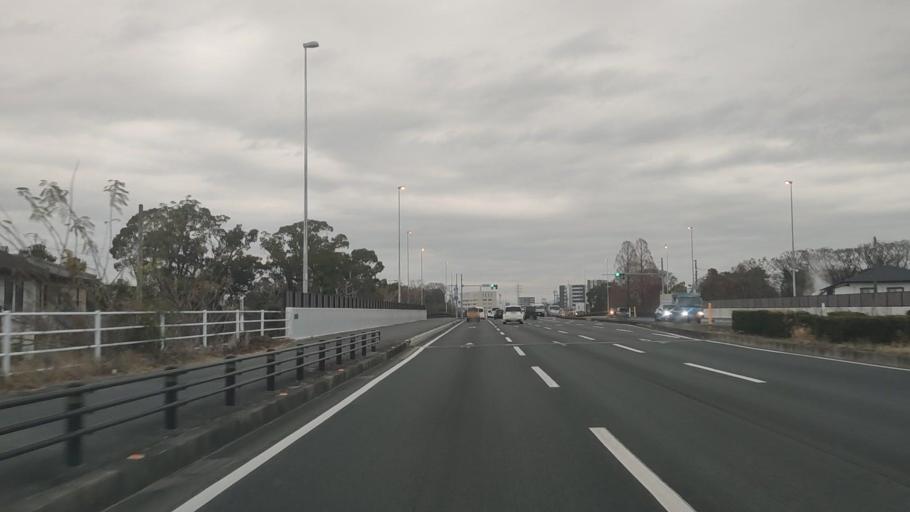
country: JP
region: Kumamoto
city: Kumamoto
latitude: 32.7761
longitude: 130.7379
